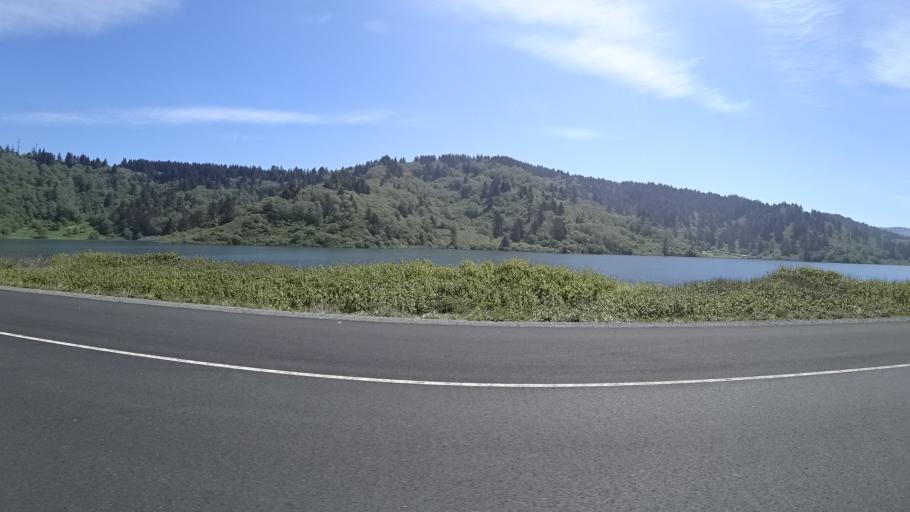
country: US
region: California
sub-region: Humboldt County
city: Westhaven-Moonstone
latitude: 41.2708
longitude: -124.0958
